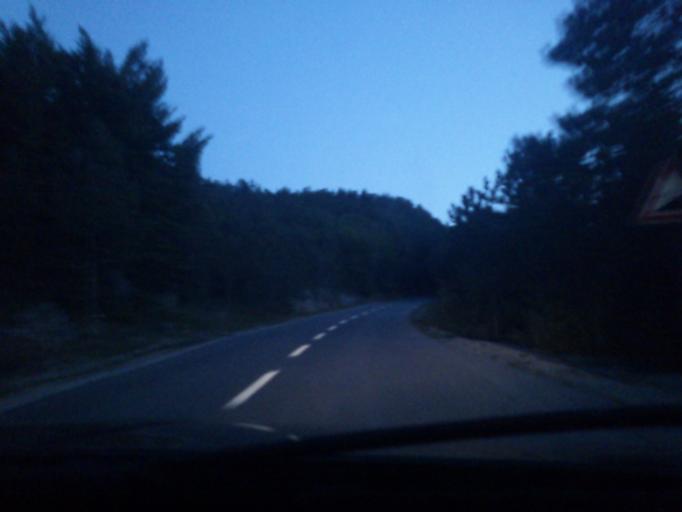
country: HR
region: Licko-Senjska
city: Senj
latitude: 44.8784
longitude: 14.9821
